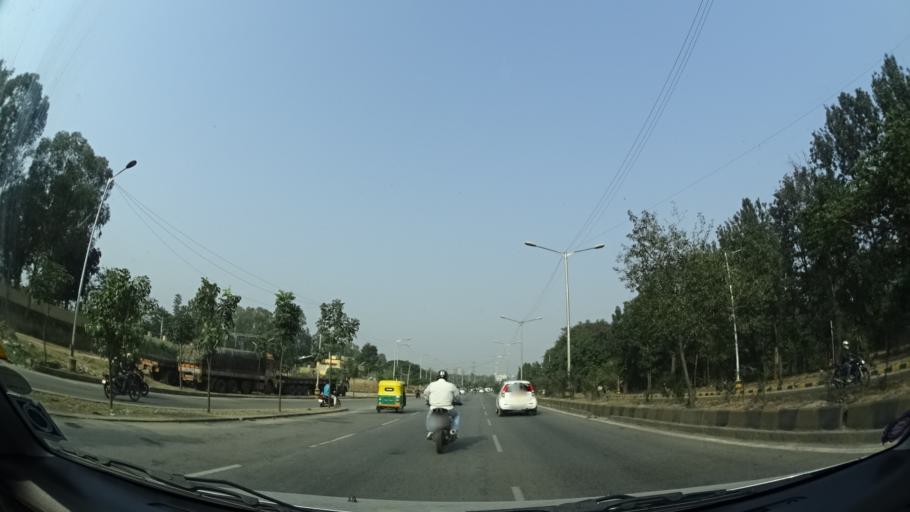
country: IN
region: Karnataka
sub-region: Bangalore Urban
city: Yelahanka
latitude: 13.0429
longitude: 77.5872
